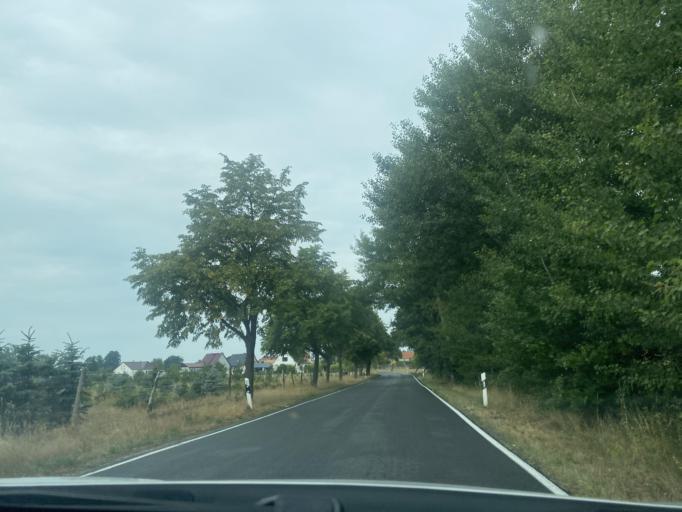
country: DE
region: Saxony
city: Wittichenau
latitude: 51.3511
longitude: 14.2840
